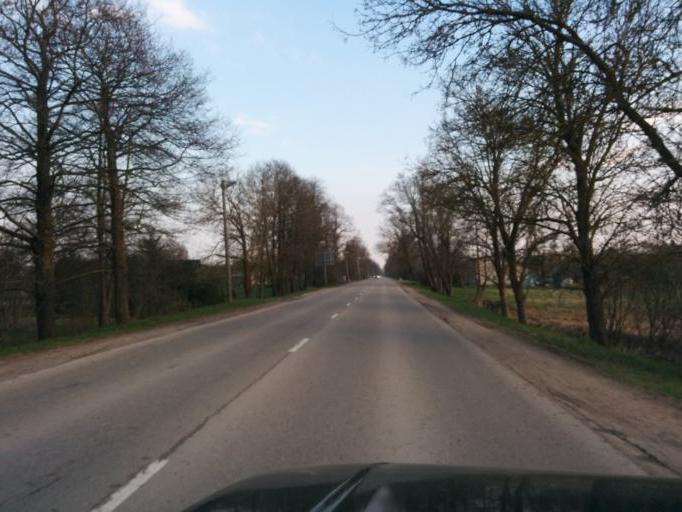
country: LV
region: Jelgava
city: Jelgava
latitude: 56.6686
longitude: 23.7316
